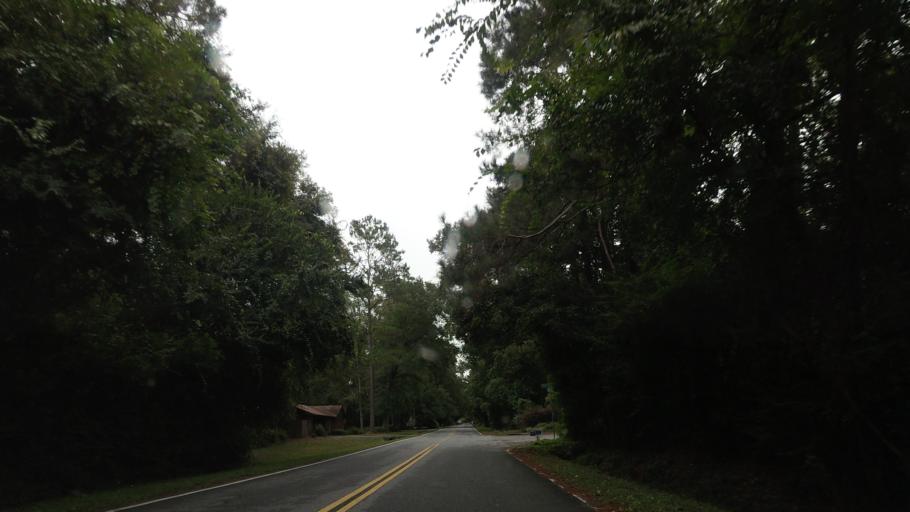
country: US
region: Georgia
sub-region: Lowndes County
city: Remerton
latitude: 30.8853
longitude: -83.3119
